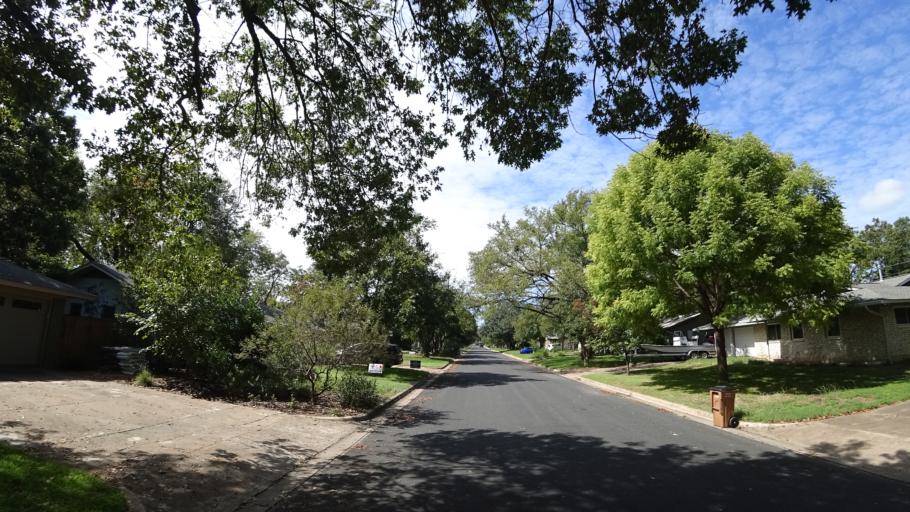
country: US
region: Texas
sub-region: Travis County
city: Austin
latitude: 30.3405
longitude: -97.7335
